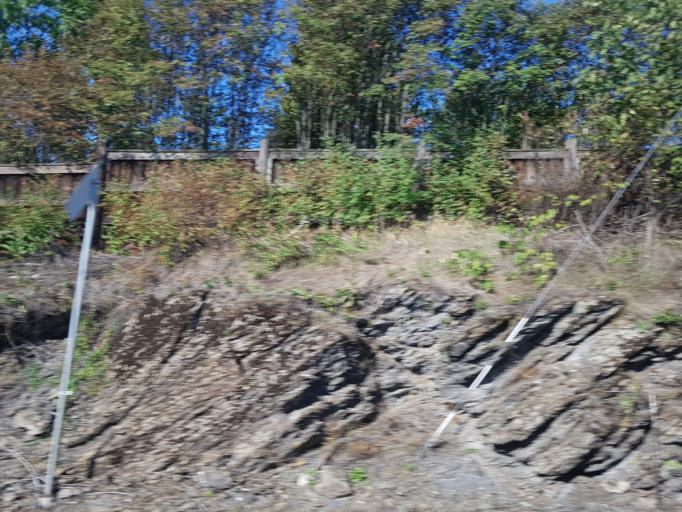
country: NO
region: Akershus
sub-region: Baerum
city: Lysaker
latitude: 59.9167
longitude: 10.6528
